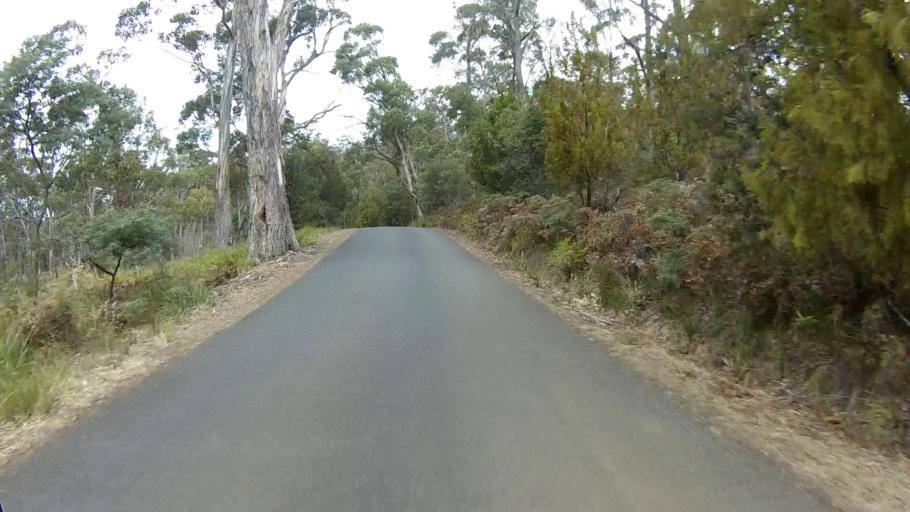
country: AU
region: Tasmania
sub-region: Sorell
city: Sorell
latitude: -42.6042
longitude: 147.9216
